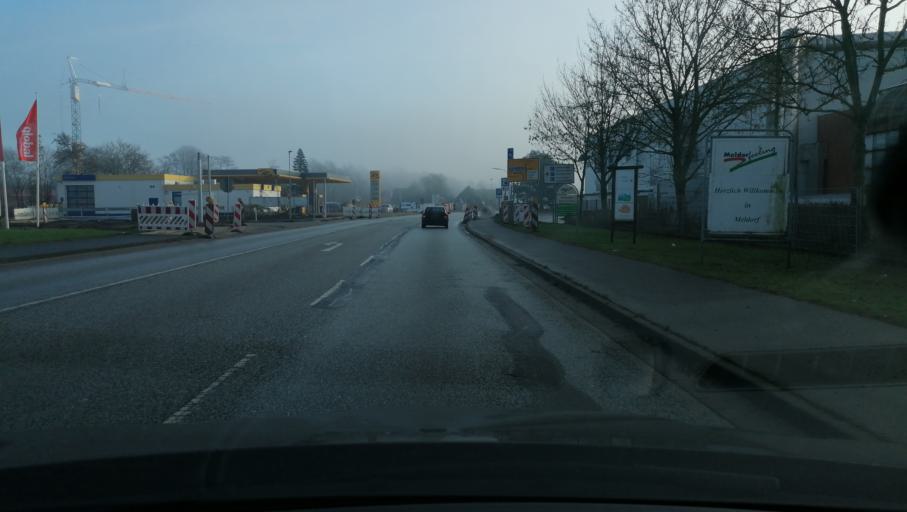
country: DE
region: Schleswig-Holstein
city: Meldorf
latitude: 54.0972
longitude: 9.0628
